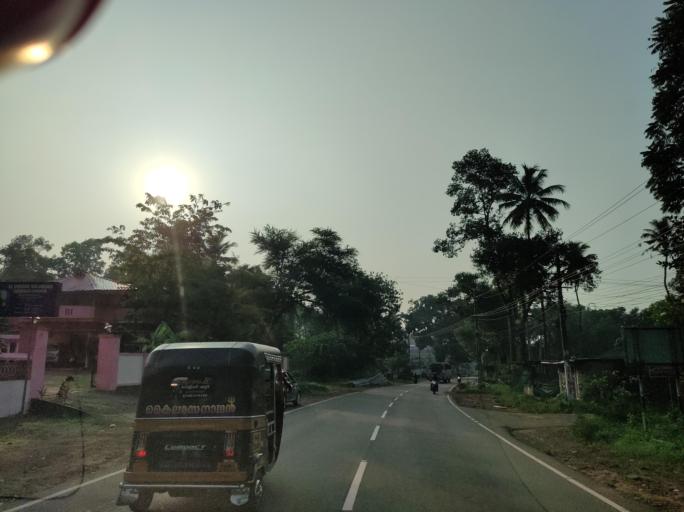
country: IN
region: Kerala
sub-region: Pattanamtitta
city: Adur
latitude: 9.1728
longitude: 76.6481
